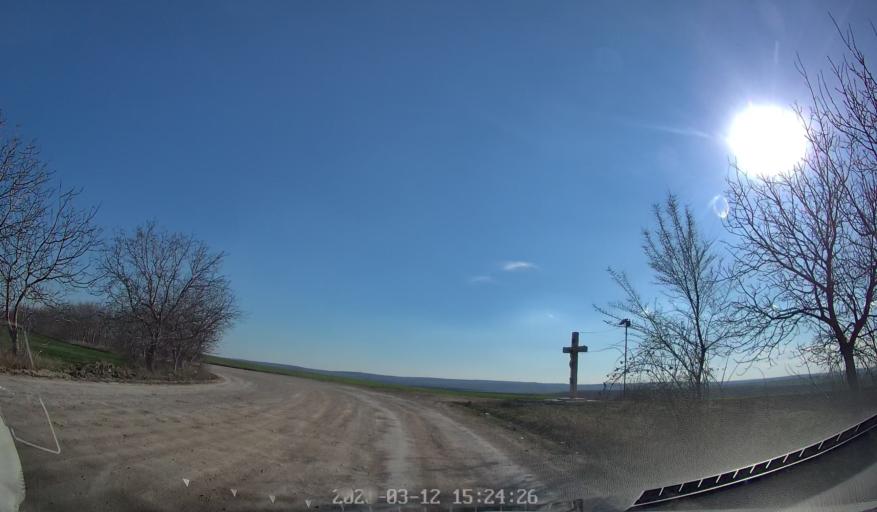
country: MD
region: Chisinau
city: Ciorescu
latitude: 47.1867
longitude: 28.9135
